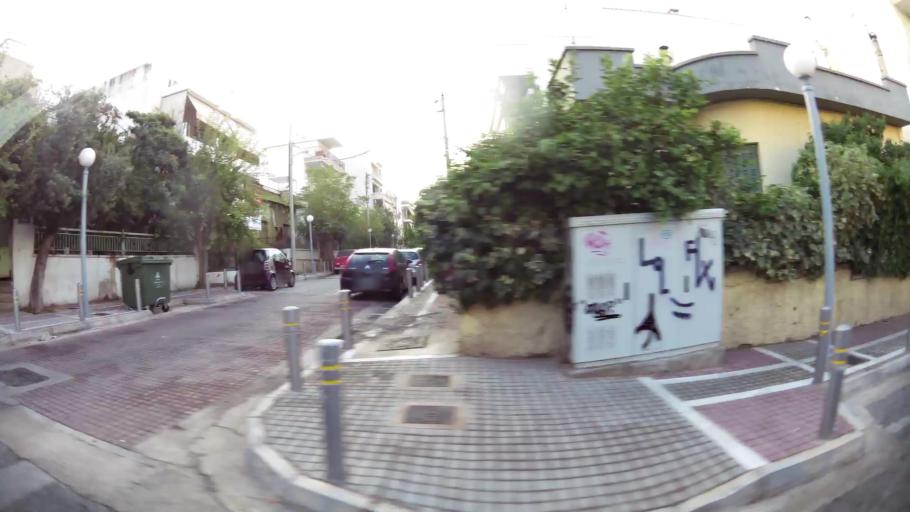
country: GR
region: Attica
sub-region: Nomarchia Athinas
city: Ymittos
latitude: 37.9486
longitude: 23.7470
